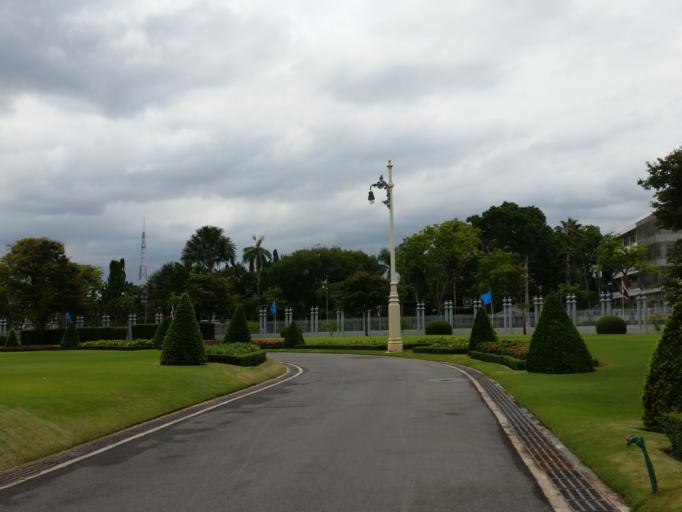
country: TH
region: Bangkok
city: Dusit
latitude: 13.7707
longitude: 100.5136
